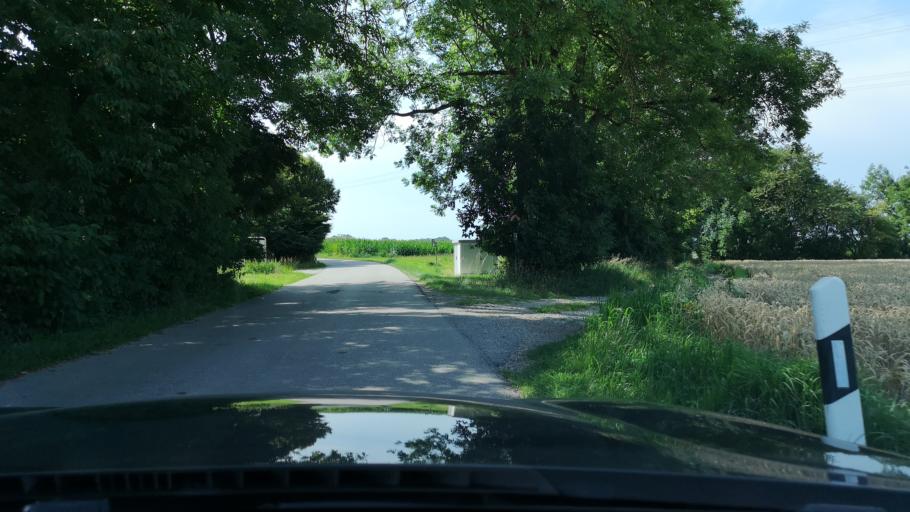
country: DE
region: Bavaria
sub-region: Upper Bavaria
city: Pliening
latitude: 48.2064
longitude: 11.7791
